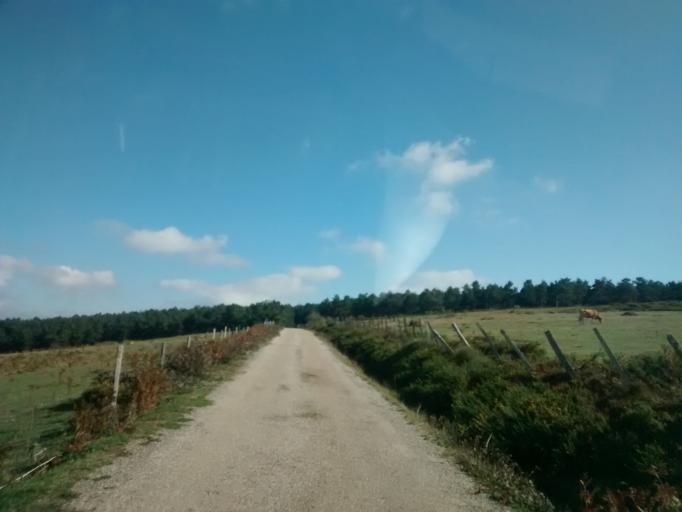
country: ES
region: Castille and Leon
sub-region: Provincia de Burgos
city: Arija
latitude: 42.9244
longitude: -3.9894
